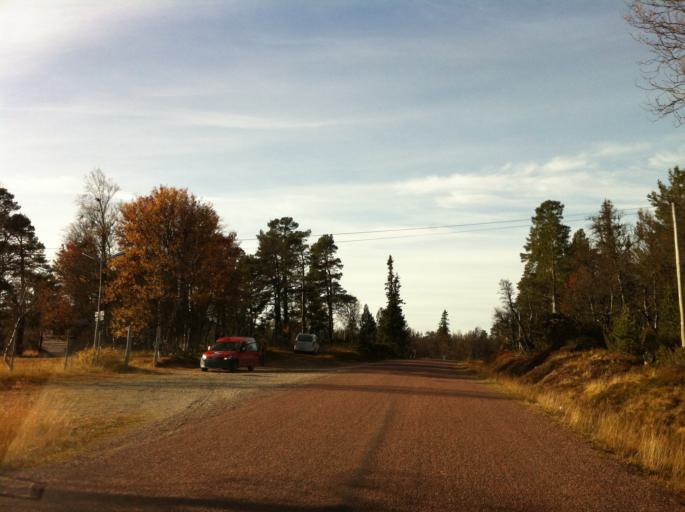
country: NO
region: Hedmark
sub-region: Engerdal
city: Engerdal
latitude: 62.0757
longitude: 12.1773
